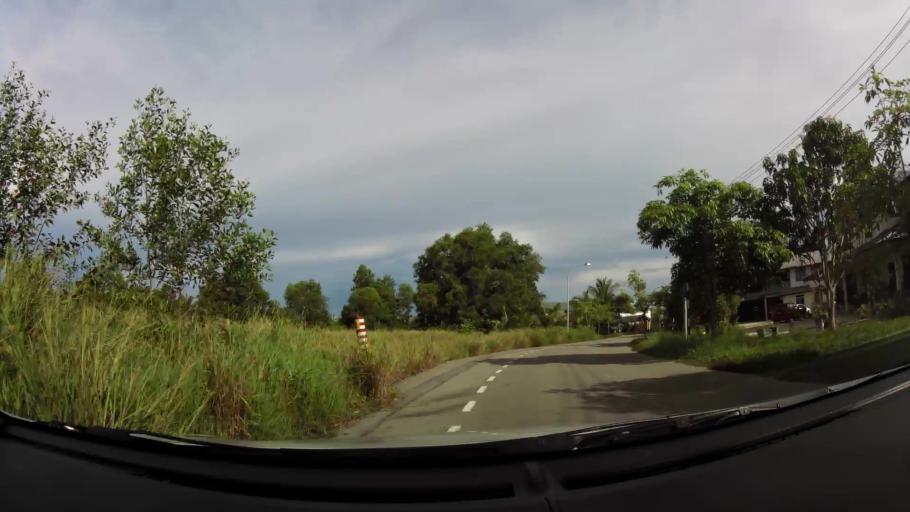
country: BN
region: Brunei and Muara
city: Bandar Seri Begawan
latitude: 4.9713
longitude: 115.0267
